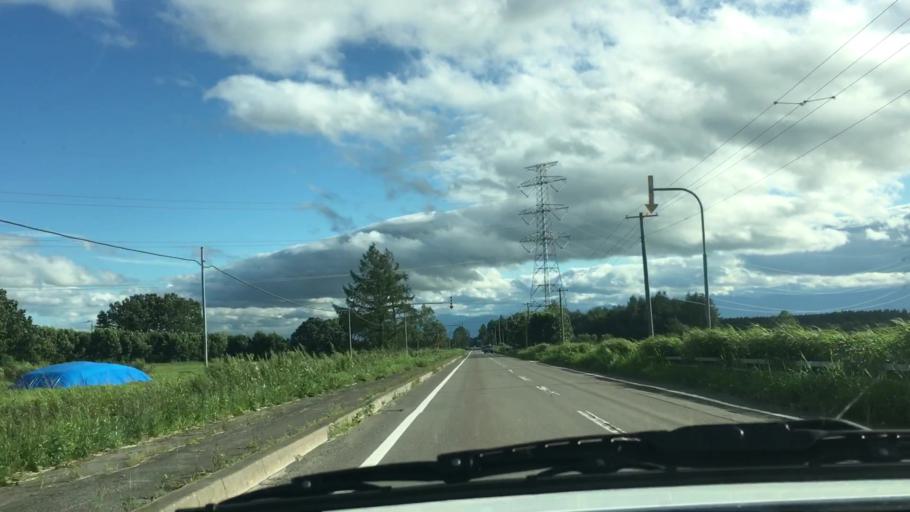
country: JP
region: Hokkaido
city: Otofuke
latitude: 43.1765
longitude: 143.0072
